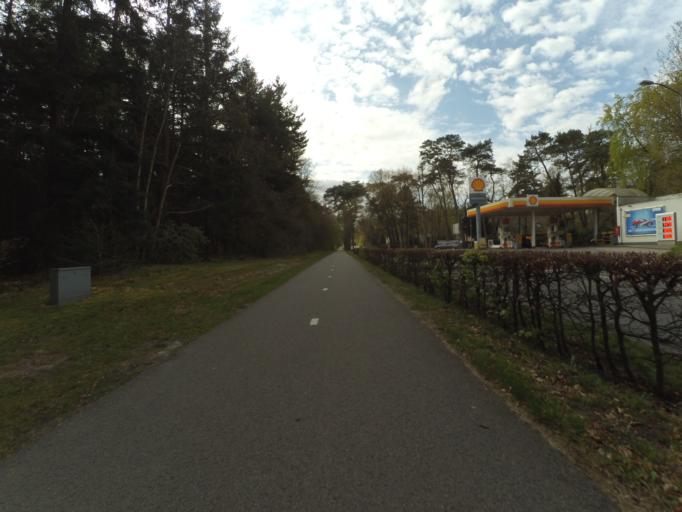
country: NL
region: Gelderland
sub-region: Gemeente Nunspeet
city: Nunspeet
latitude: 52.3658
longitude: 5.7846
